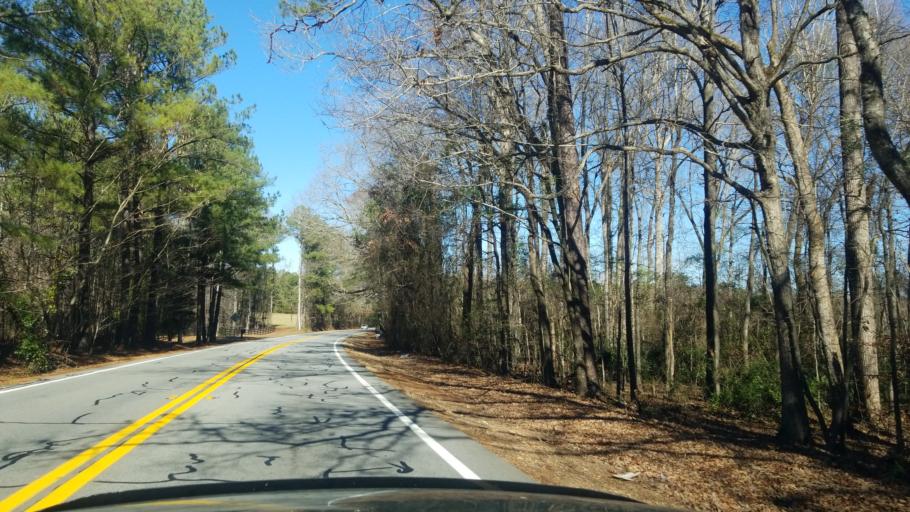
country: US
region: Georgia
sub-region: Harris County
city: Hamilton
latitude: 32.6757
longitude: -84.8592
